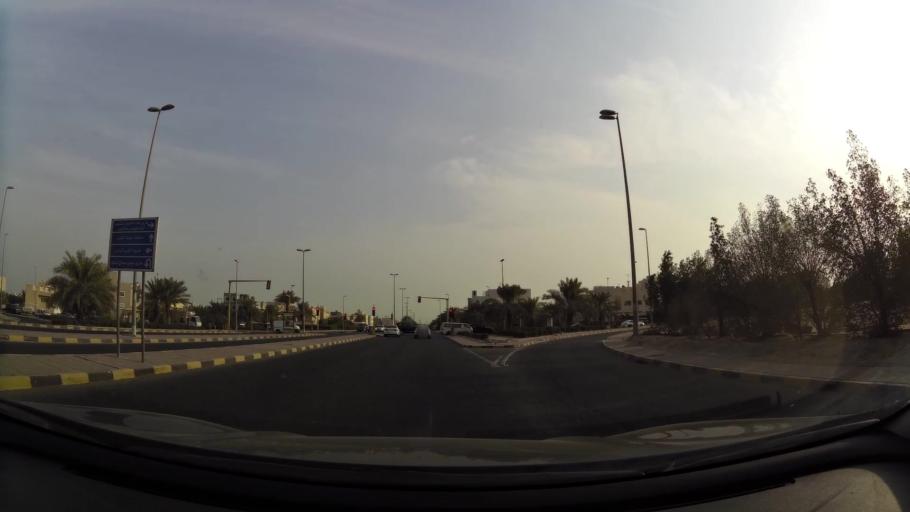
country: KW
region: Mubarak al Kabir
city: Mubarak al Kabir
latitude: 29.1946
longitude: 48.0690
